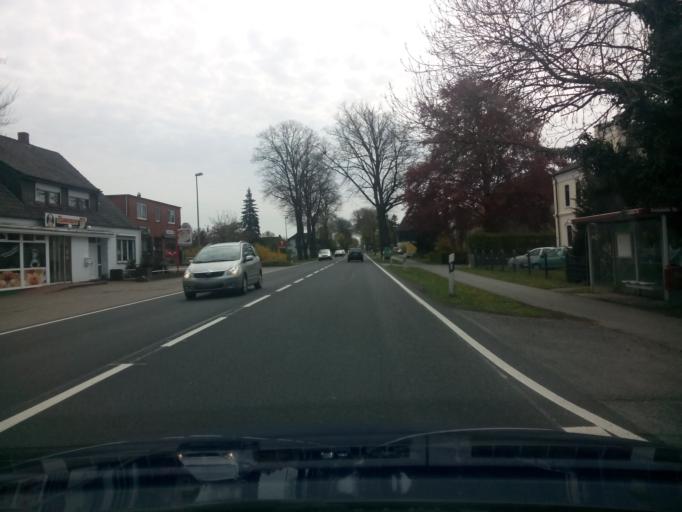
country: DE
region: Lower Saxony
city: Stuhr
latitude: 52.9959
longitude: 8.7870
